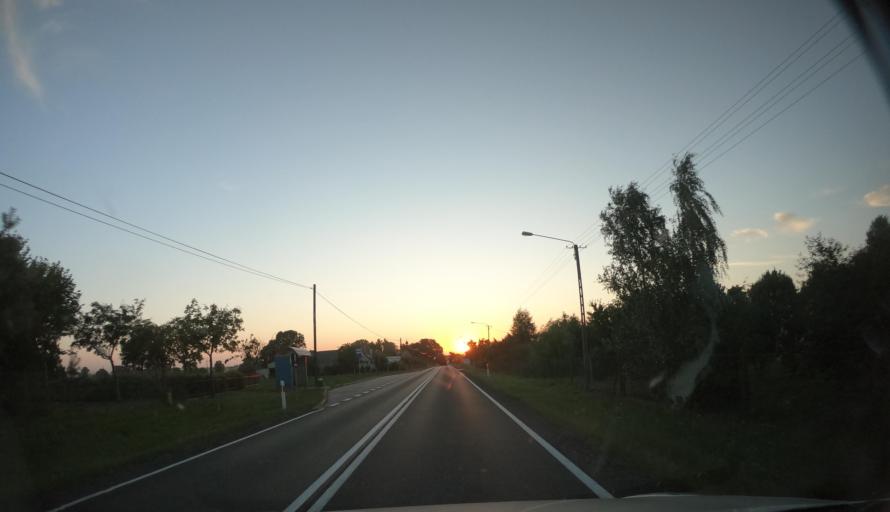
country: PL
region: Kujawsko-Pomorskie
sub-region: Powiat bydgoski
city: Koronowo
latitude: 53.3434
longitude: 17.8668
